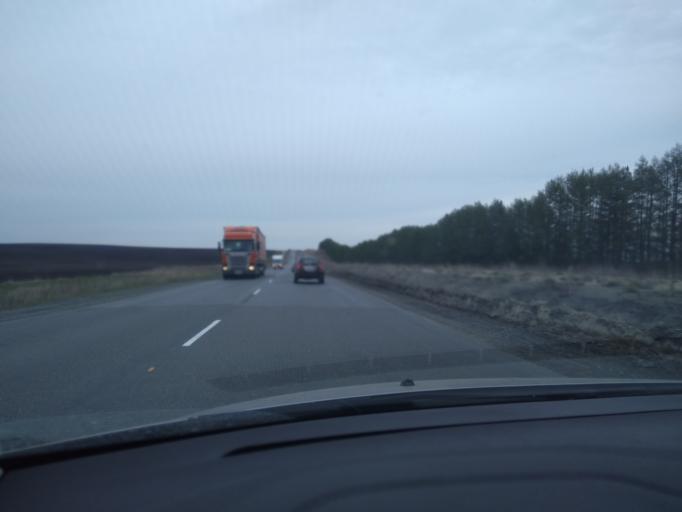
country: RU
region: Sverdlovsk
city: Kamyshlov
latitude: 56.8593
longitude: 62.8924
